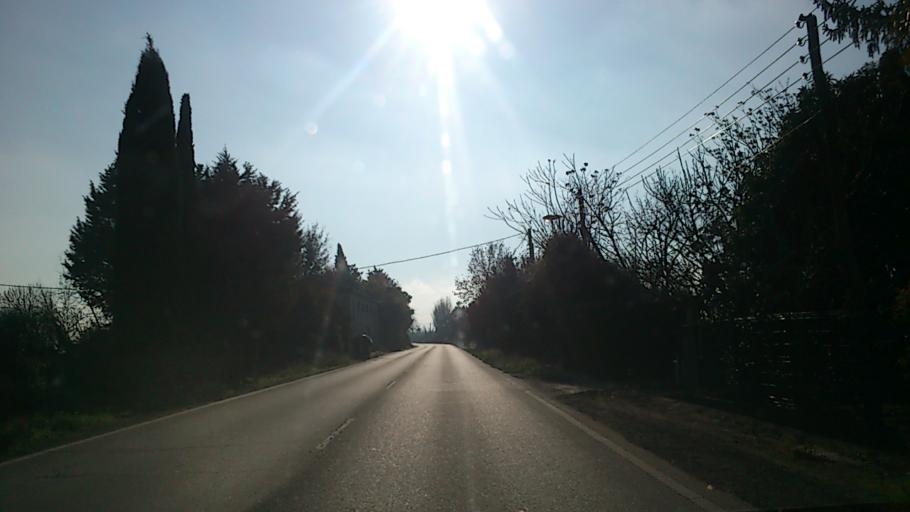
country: ES
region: Aragon
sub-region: Provincia de Zaragoza
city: Villanueva de Gallego
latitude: 41.7130
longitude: -0.8116
